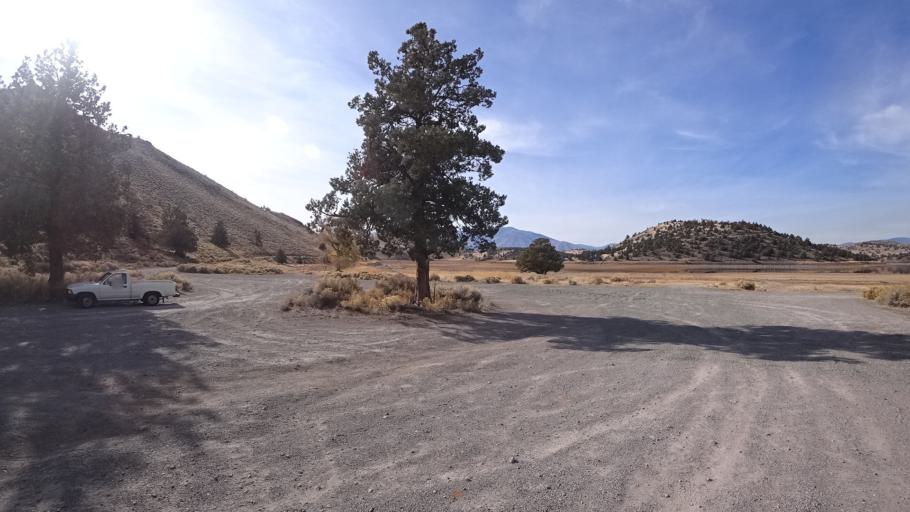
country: US
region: California
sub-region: Siskiyou County
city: Weed
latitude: 41.5048
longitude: -122.3928
